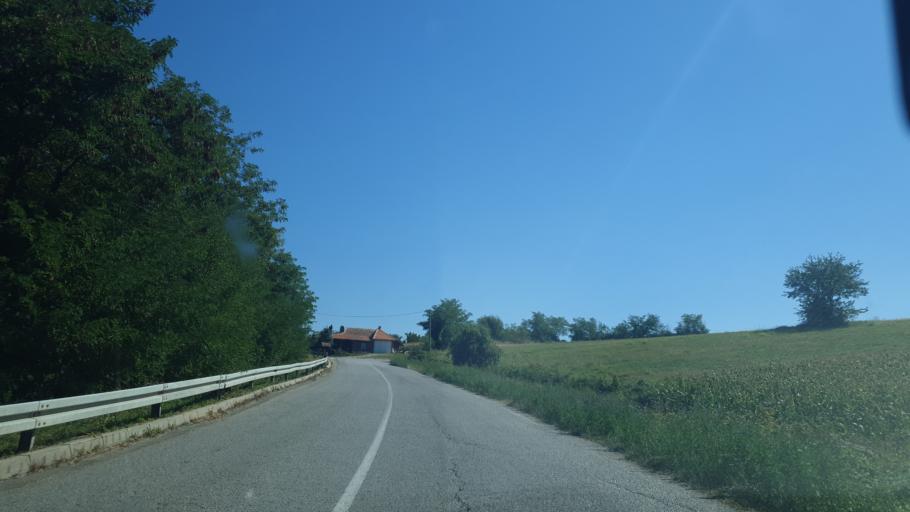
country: RS
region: Central Serbia
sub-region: Kolubarski Okrug
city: Mionica
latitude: 44.2234
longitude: 20.0846
